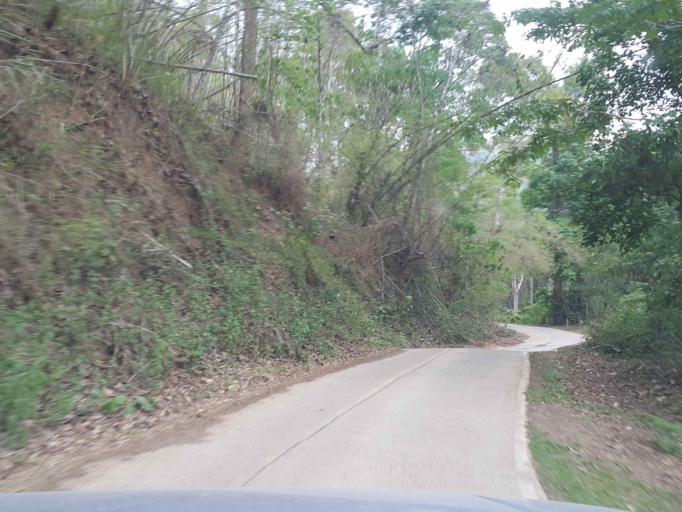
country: TH
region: Chiang Mai
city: Wiang Haeng
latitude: 19.3781
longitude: 98.7500
